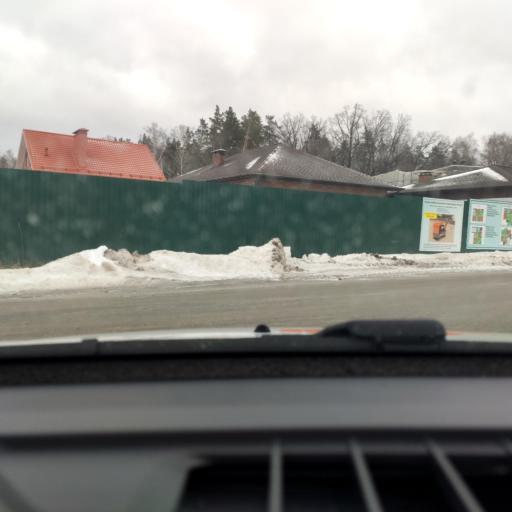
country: RU
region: Voronezj
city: Podgornoye
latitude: 51.7551
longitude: 39.1503
